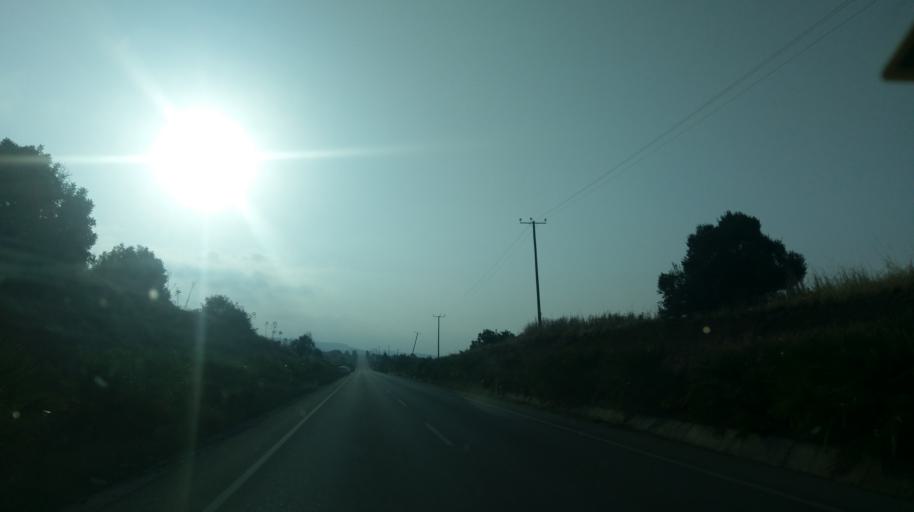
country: CY
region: Ammochostos
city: Trikomo
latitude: 35.4360
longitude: 33.9465
